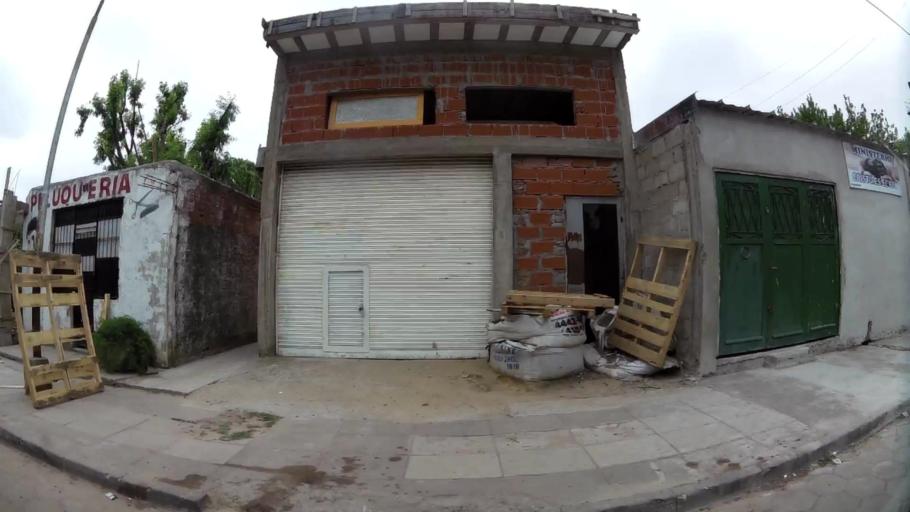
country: AR
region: Buenos Aires
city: San Justo
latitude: -34.7035
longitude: -58.5396
